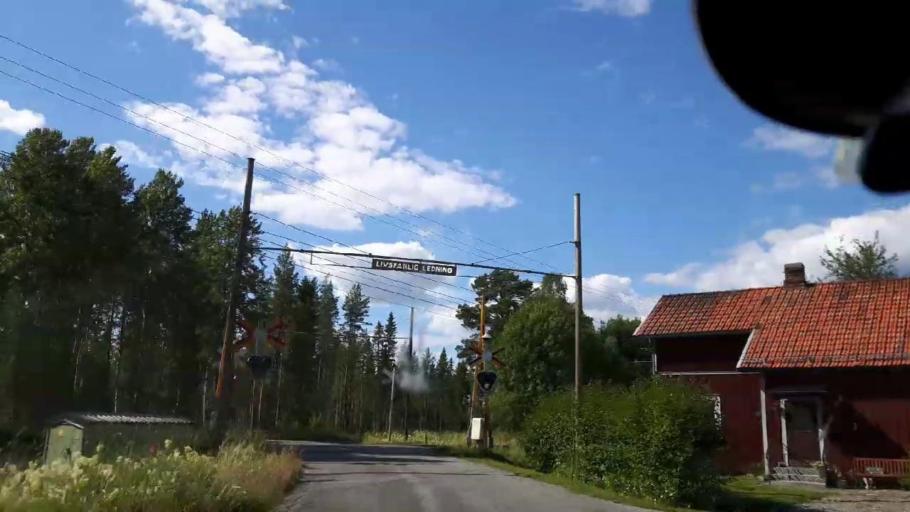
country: SE
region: Jaemtland
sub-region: Braecke Kommun
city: Braecke
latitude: 62.8399
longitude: 15.3007
